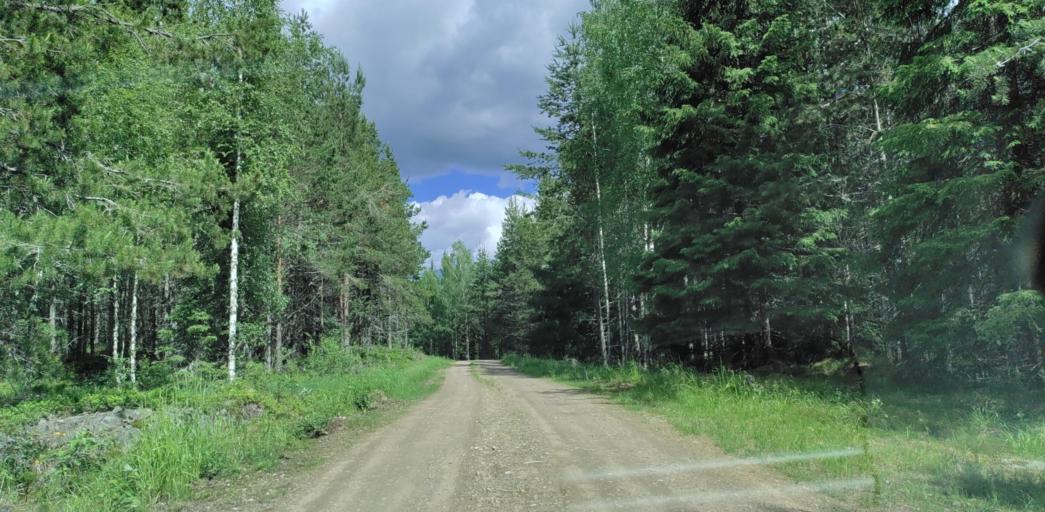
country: SE
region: Vaermland
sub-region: Hagfors Kommun
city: Ekshaerad
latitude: 60.1190
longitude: 13.3261
